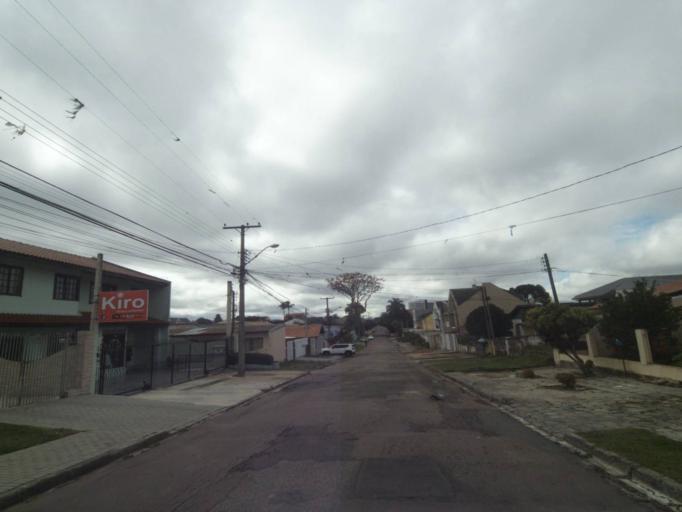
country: BR
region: Parana
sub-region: Curitiba
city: Curitiba
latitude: -25.4983
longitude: -49.2858
